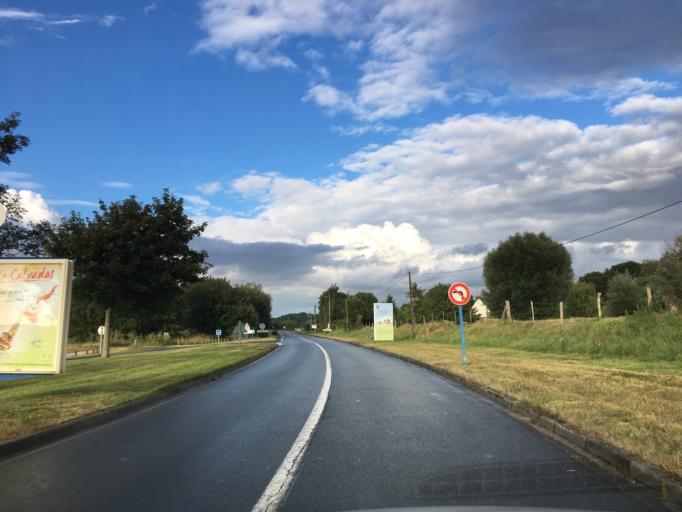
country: FR
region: Lower Normandy
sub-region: Departement du Calvados
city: Amfreville
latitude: 49.2649
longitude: -0.2257
